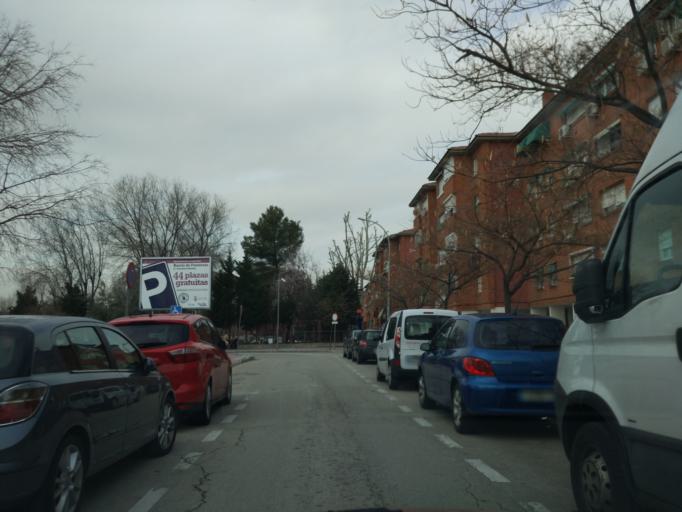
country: ES
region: Madrid
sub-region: Provincia de Madrid
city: Torrejon de Ardoz
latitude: 40.4593
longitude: -3.4860
